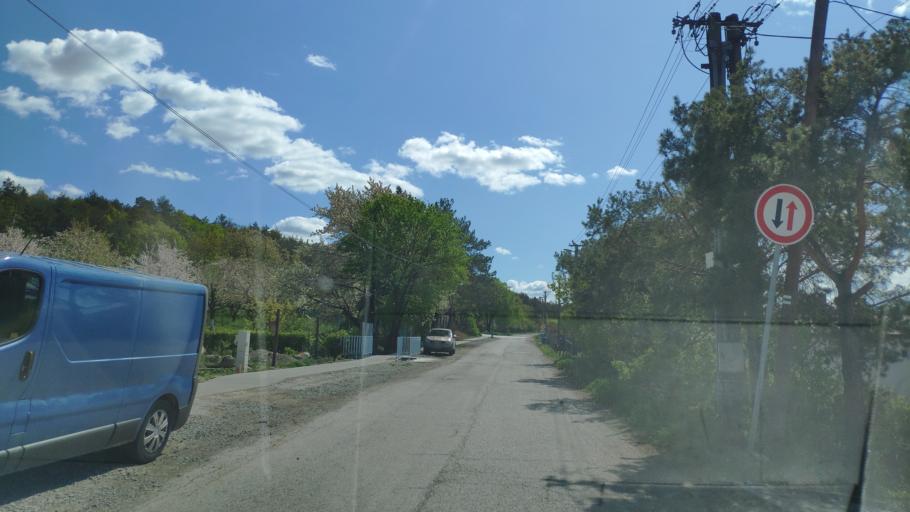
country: SK
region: Kosicky
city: Kosice
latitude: 48.6761
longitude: 21.4306
